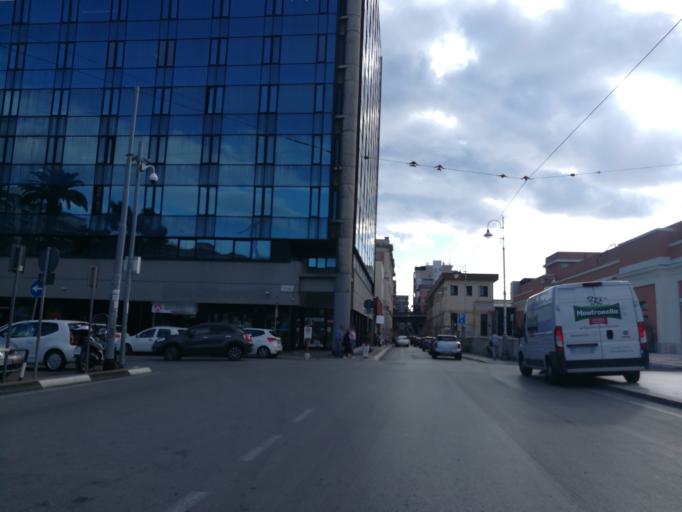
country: IT
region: Apulia
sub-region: Provincia di Bari
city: Bari
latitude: 41.1182
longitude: 16.8707
